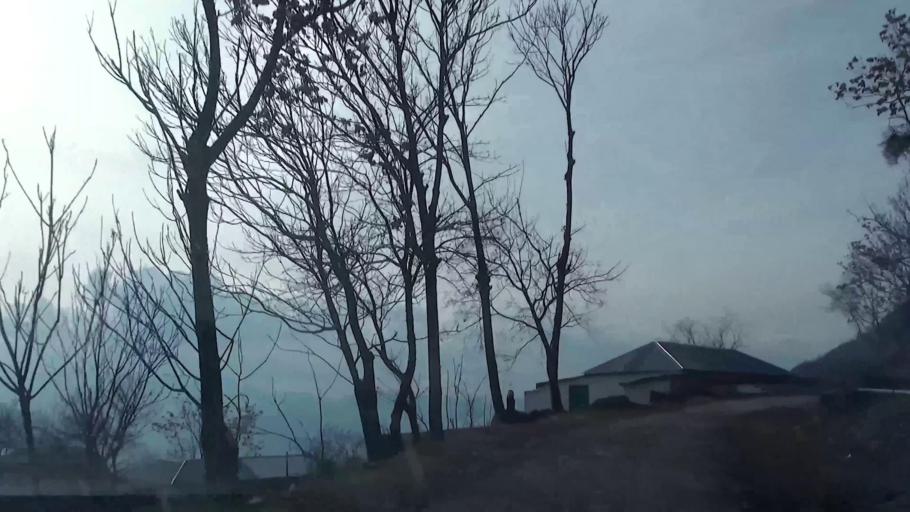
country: PK
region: Azad Kashmir
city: Muzaffarabad
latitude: 34.3671
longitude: 73.5256
